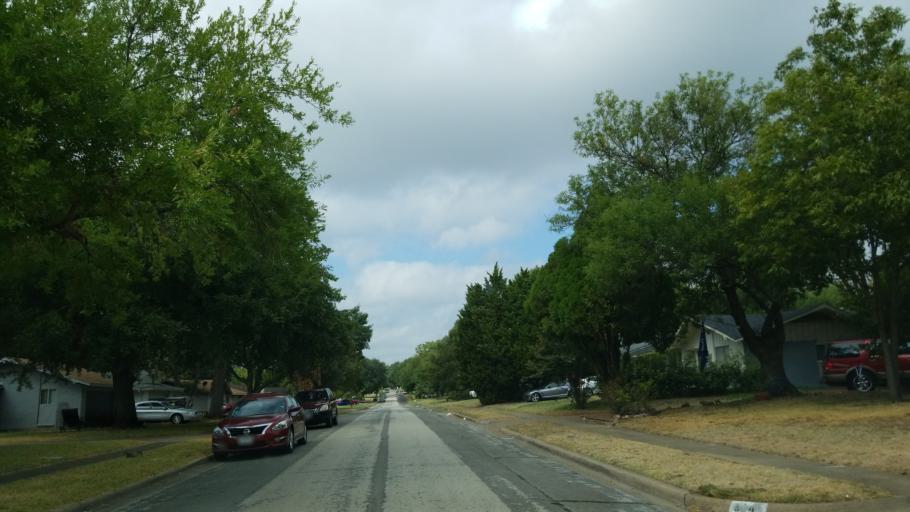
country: US
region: Texas
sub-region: Dallas County
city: Richardson
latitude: 32.9381
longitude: -96.7654
